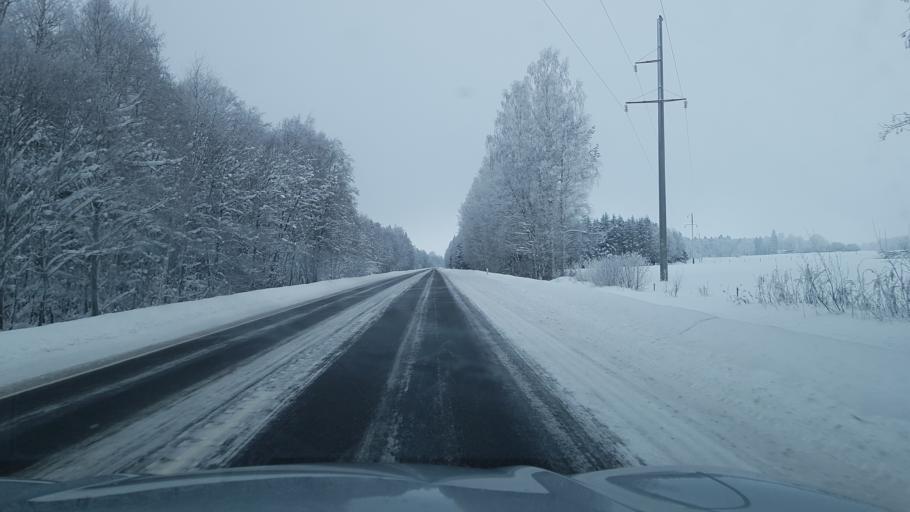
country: EE
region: Ida-Virumaa
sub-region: Johvi vald
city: Johvi
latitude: 59.2990
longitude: 27.3966
